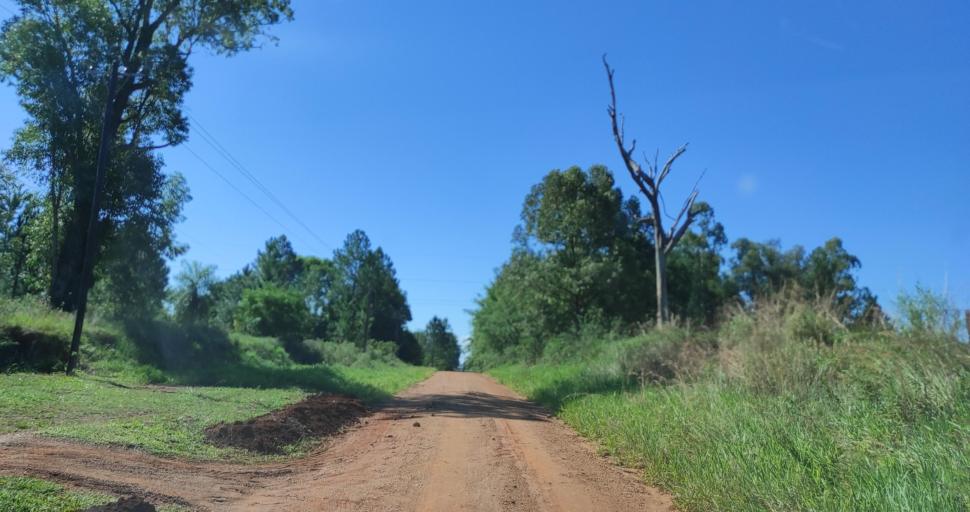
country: AR
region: Misiones
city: Garupa
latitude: -27.4694
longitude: -55.7980
